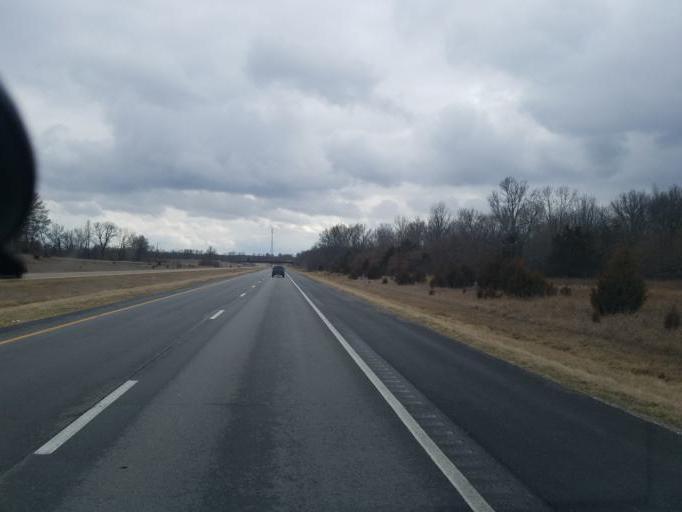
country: US
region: Missouri
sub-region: Randolph County
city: Moberly
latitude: 39.3036
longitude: -92.3737
